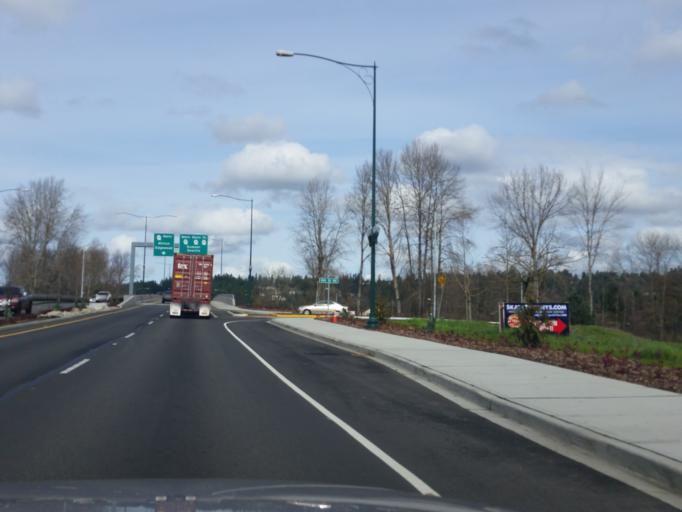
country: US
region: Washington
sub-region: Pierce County
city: North Puyallup
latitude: 47.2008
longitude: -122.2938
